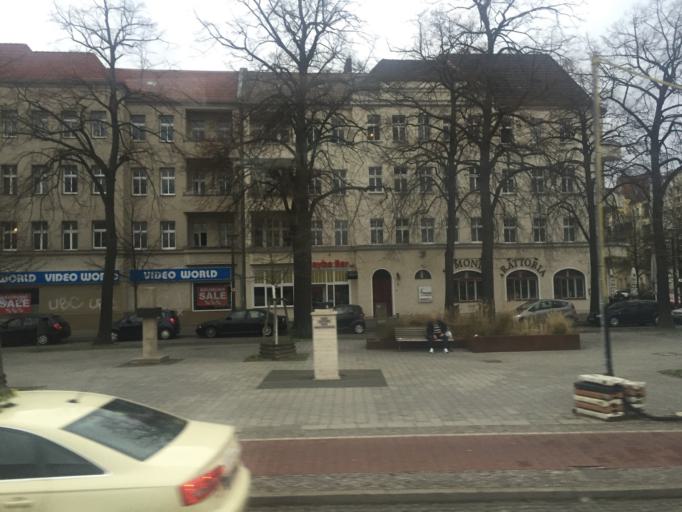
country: DE
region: Berlin
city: Adlershof
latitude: 52.4345
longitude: 13.5425
